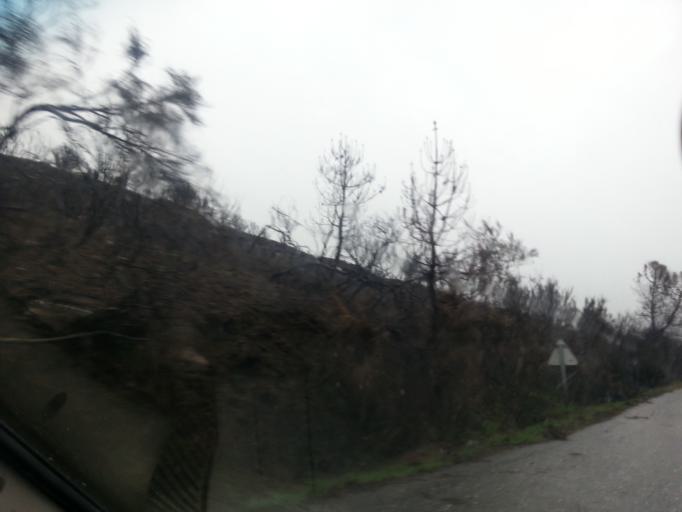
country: PT
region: Guarda
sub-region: Celorico da Beira
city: Celorico da Beira
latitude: 40.5415
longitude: -7.4461
